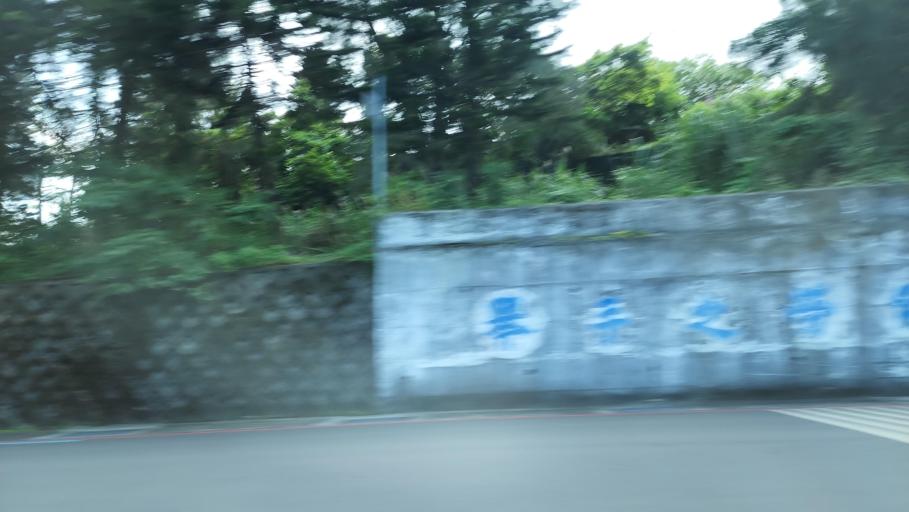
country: TW
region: Taiwan
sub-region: Keelung
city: Keelung
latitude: 25.2233
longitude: 121.6441
